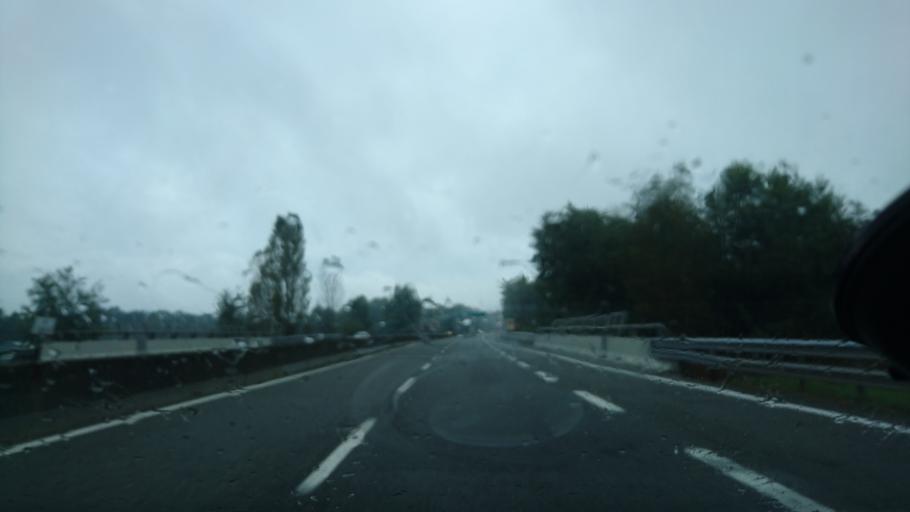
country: IT
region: Piedmont
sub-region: Provincia di Novara
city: Paruzzaro
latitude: 45.7311
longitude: 8.5112
